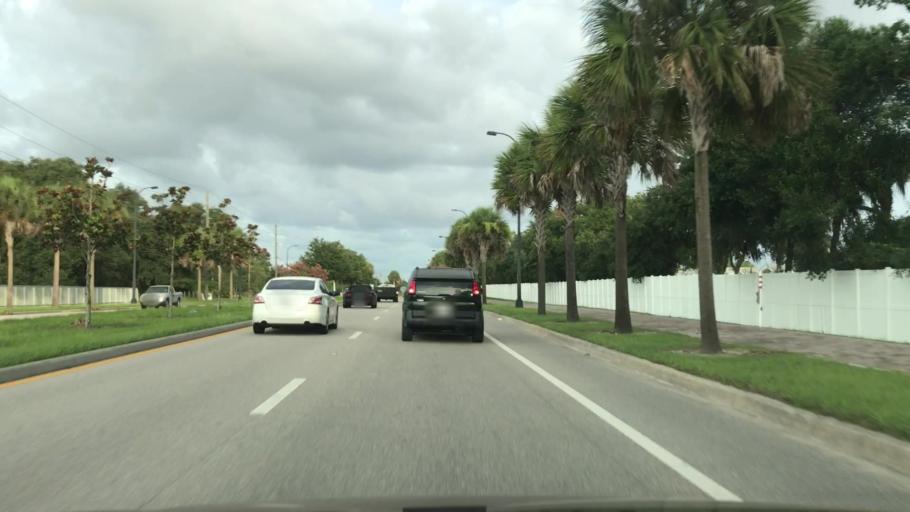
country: US
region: Florida
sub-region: Sarasota County
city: Fruitville
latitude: 27.3383
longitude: -82.4205
